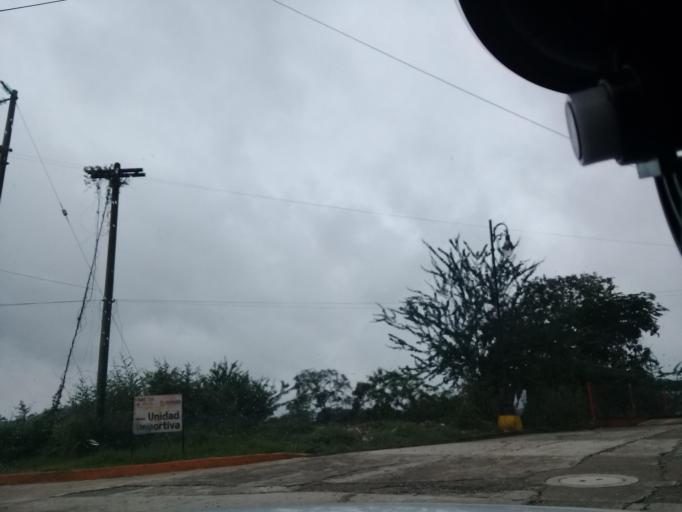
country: MX
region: Veracruz
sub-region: Chalma
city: San Pedro Coyutla
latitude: 21.2072
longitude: -98.3954
